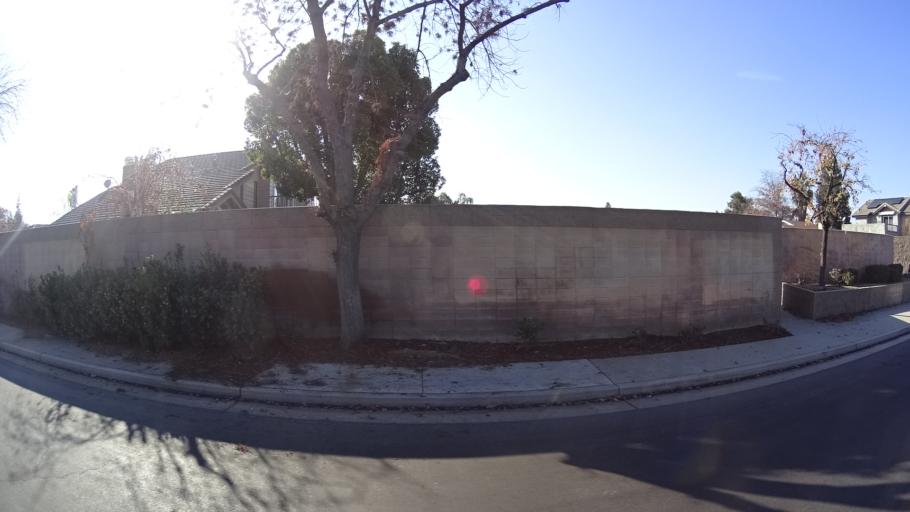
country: US
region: California
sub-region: Kern County
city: Greenacres
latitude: 35.3176
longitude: -119.1048
